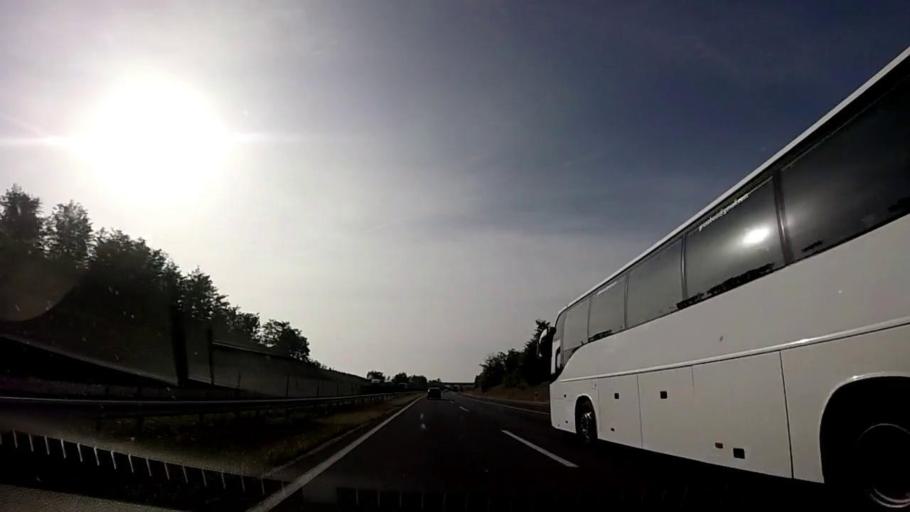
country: HU
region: Somogy
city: Zamardi
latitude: 46.8423
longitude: 17.9528
